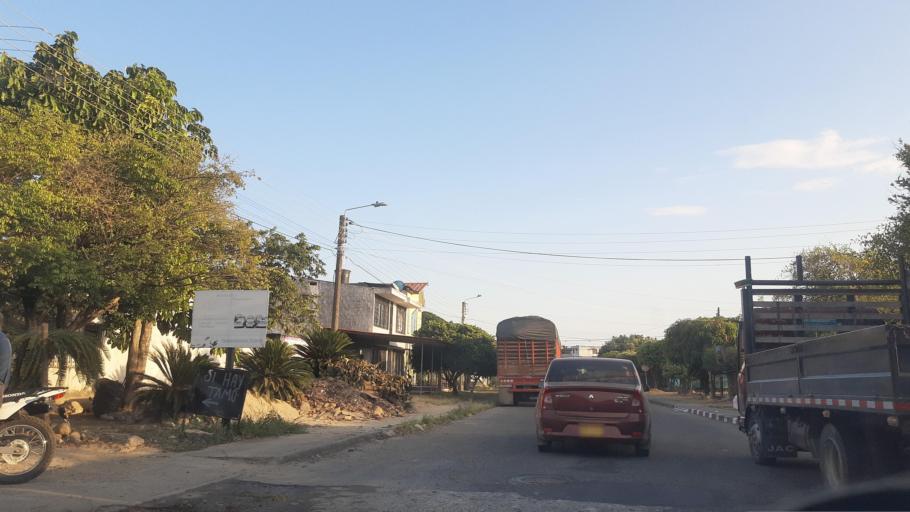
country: CO
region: Arauca
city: Tame
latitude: 6.4577
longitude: -71.7333
